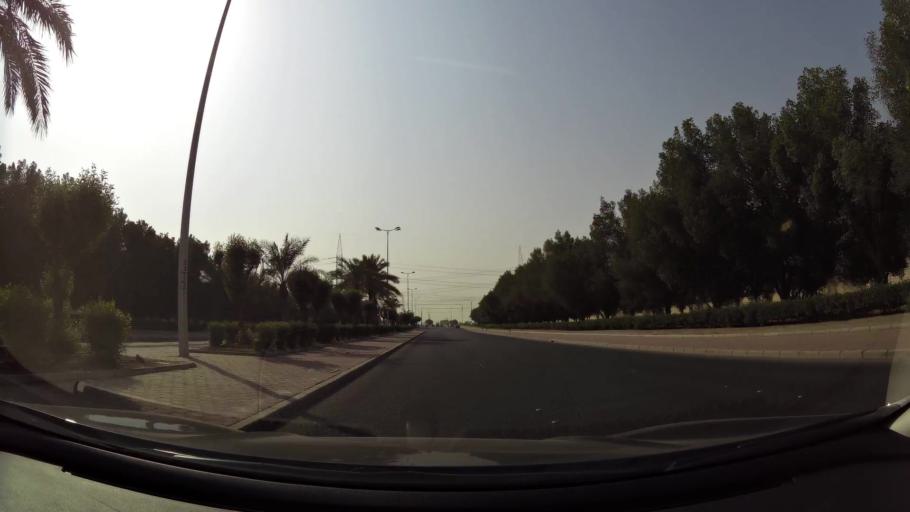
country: KW
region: Al Asimah
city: Ar Rabiyah
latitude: 29.2991
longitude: 47.8321
